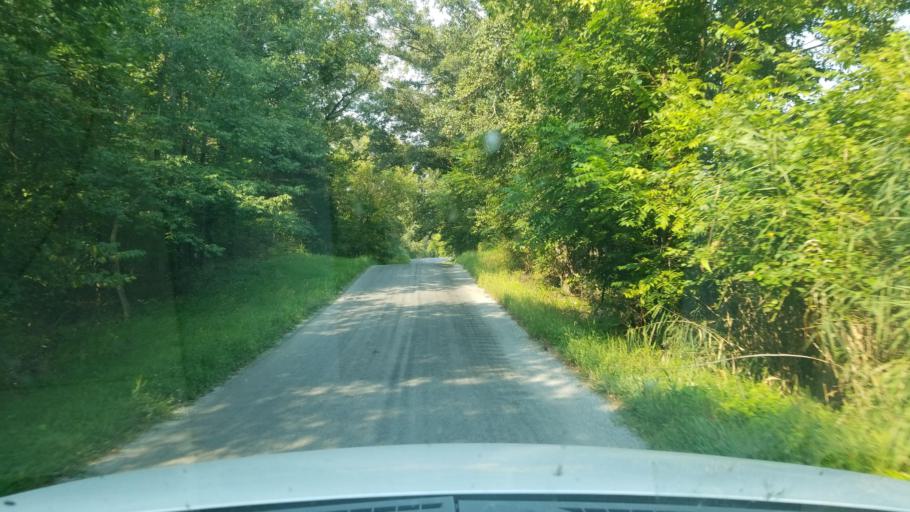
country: US
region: Illinois
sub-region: Saline County
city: Carrier Mills
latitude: 37.7904
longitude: -88.6813
